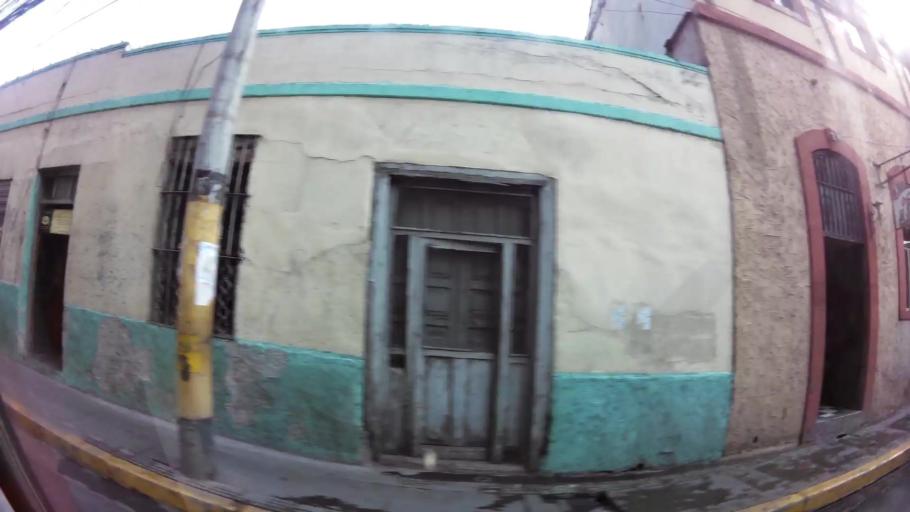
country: HN
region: Francisco Morazan
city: Tegucigalpa
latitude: 14.1051
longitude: -87.2021
